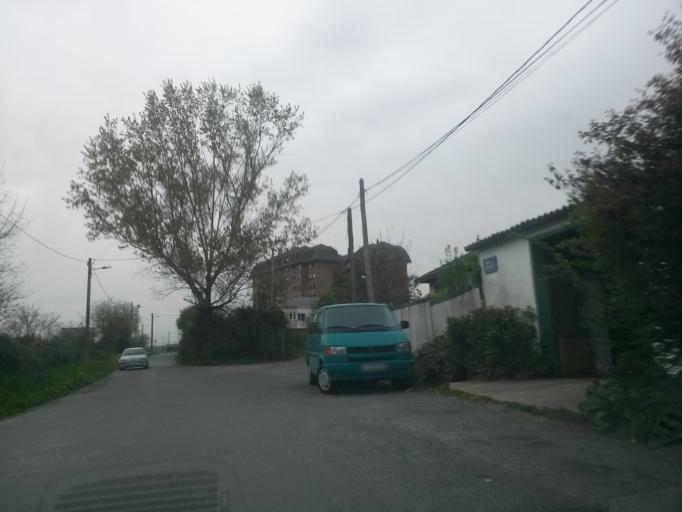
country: ES
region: Galicia
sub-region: Provincia de Lugo
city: Lugo
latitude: 43.0296
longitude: -7.5513
